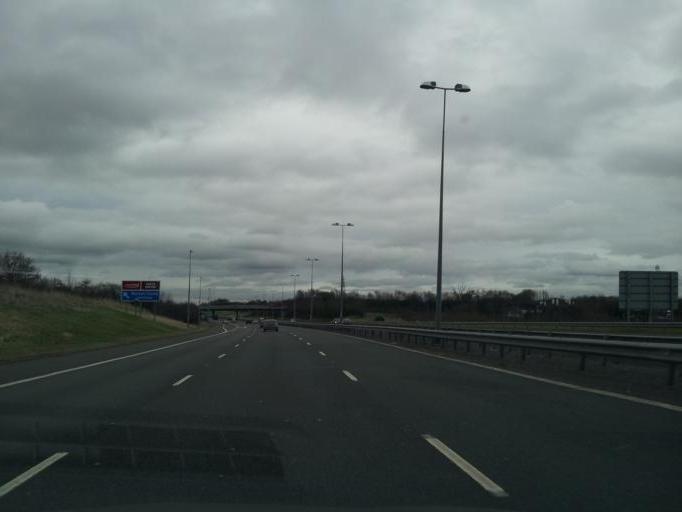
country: GB
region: England
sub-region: Staffordshire
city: Norton Canes
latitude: 52.6630
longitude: -1.9795
